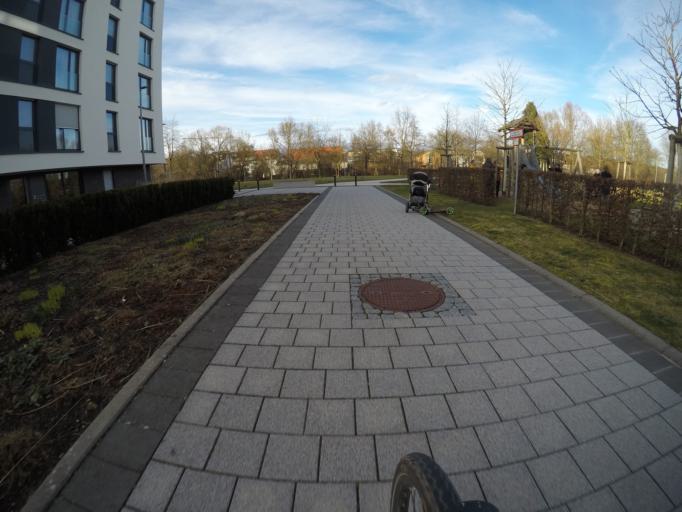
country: DE
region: Baden-Wuerttemberg
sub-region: Regierungsbezirk Stuttgart
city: Boeblingen
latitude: 48.6783
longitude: 9.0172
